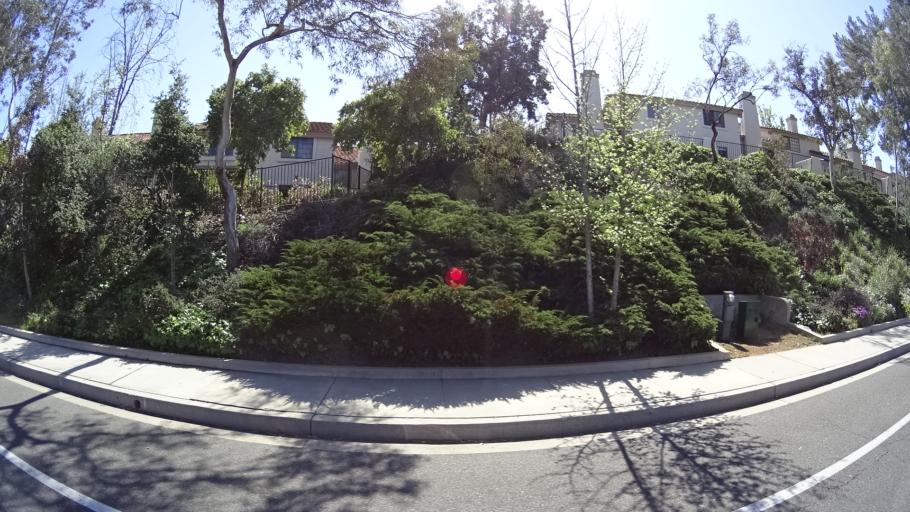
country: US
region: California
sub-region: Ventura County
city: Casa Conejo
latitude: 34.1804
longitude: -118.8928
